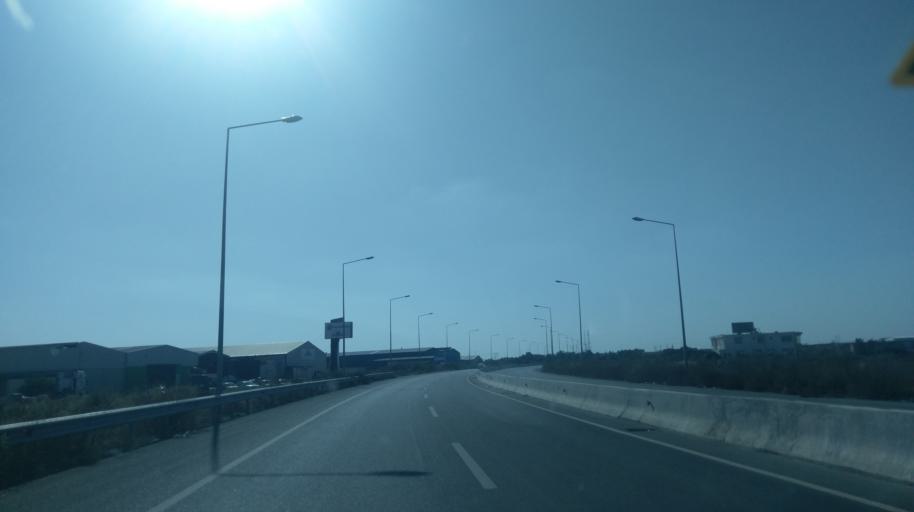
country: CY
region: Ammochostos
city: Famagusta
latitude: 35.1487
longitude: 33.8974
